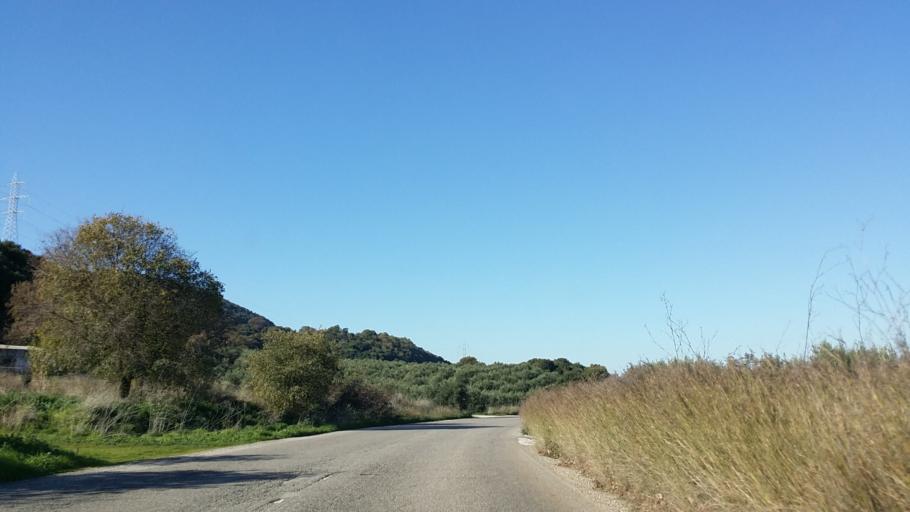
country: GR
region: West Greece
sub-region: Nomos Aitolias kai Akarnanias
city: Monastirakion
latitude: 38.8699
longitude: 21.0507
